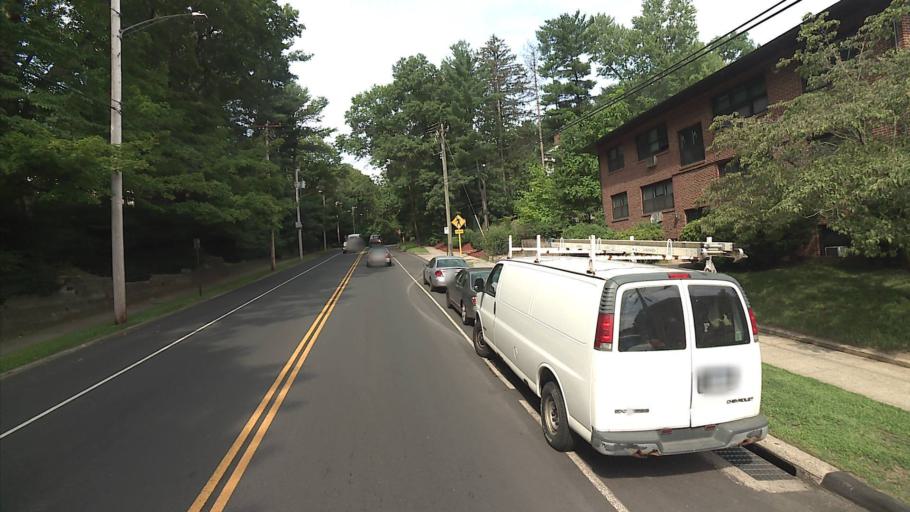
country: US
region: Connecticut
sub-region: New Haven County
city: Woodbridge
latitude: 41.3273
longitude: -72.9709
